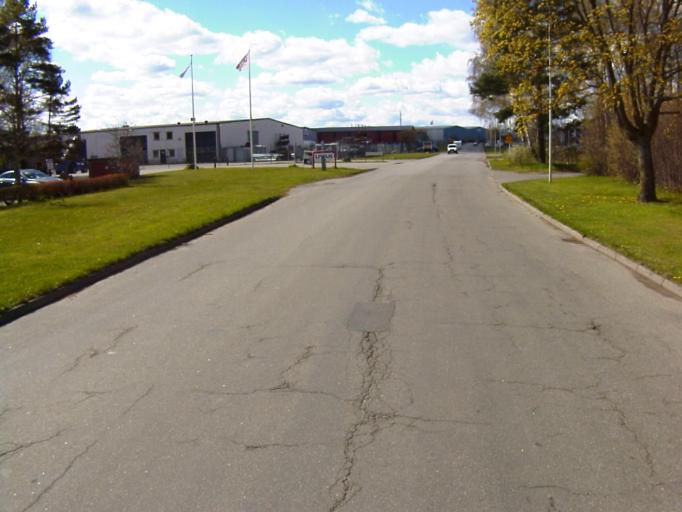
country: SE
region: Skane
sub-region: Kristianstads Kommun
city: Norra Asum
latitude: 56.0071
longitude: 14.1043
